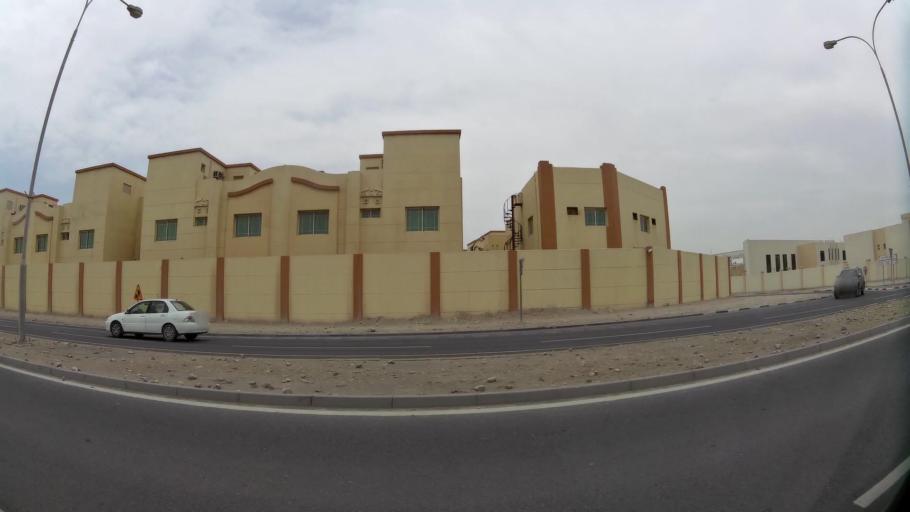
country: QA
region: Baladiyat ar Rayyan
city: Ar Rayyan
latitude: 25.2293
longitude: 51.4477
